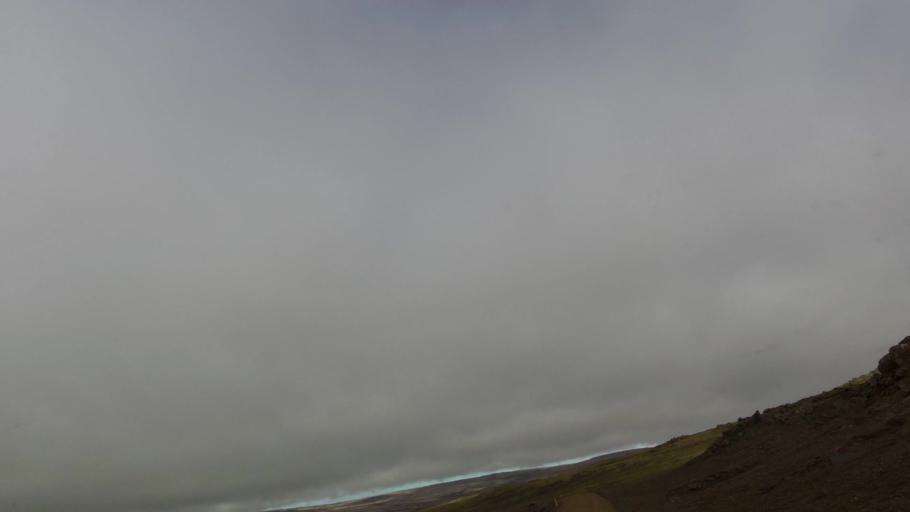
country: IS
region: West
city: Olafsvik
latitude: 65.5334
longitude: -24.3799
